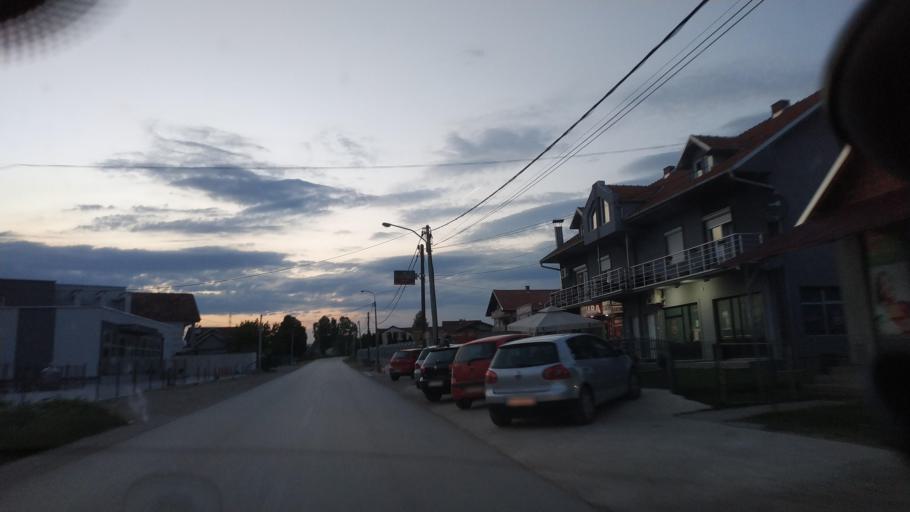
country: RS
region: Central Serbia
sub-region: Nisavski Okrug
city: Merosina
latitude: 43.2850
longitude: 21.7200
